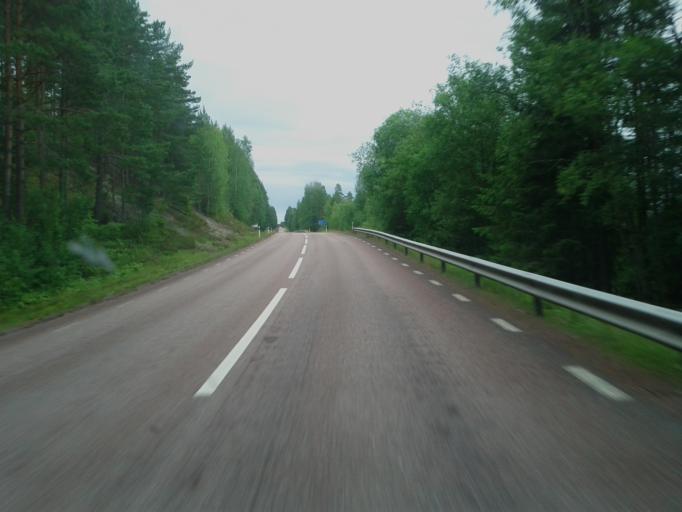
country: SE
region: Dalarna
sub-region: Mora Kommun
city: Mora
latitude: 61.0787
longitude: 14.3353
